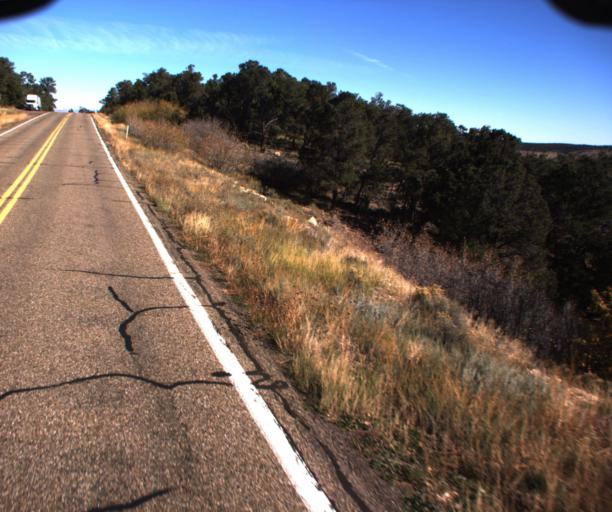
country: US
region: Arizona
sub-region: Coconino County
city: Fredonia
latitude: 36.7937
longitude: -112.2548
